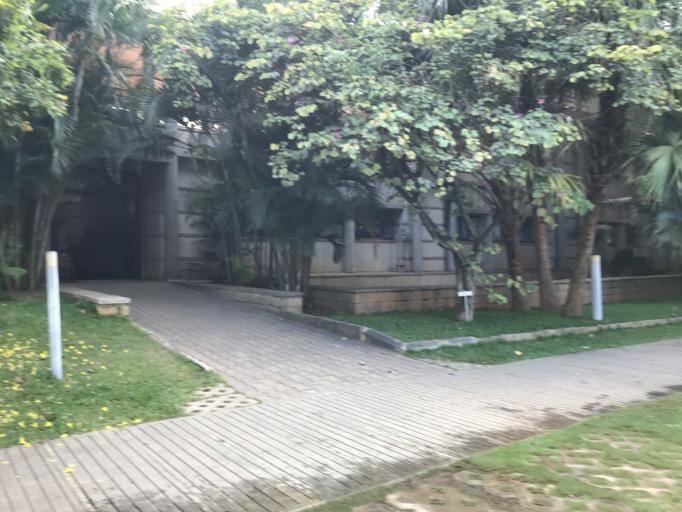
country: IN
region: Karnataka
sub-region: Bangalore Urban
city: Yelahanka
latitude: 13.0712
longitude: 77.5805
